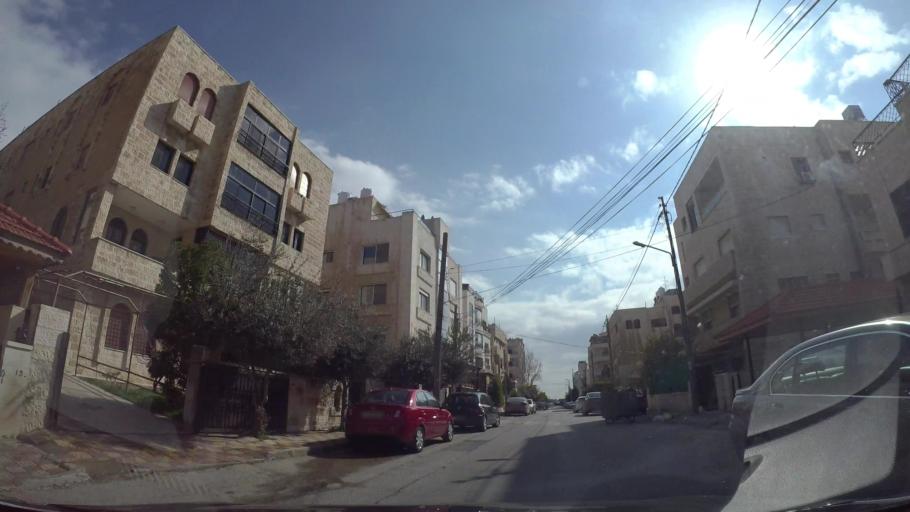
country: JO
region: Amman
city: Al Jubayhah
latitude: 31.9739
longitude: 35.8885
